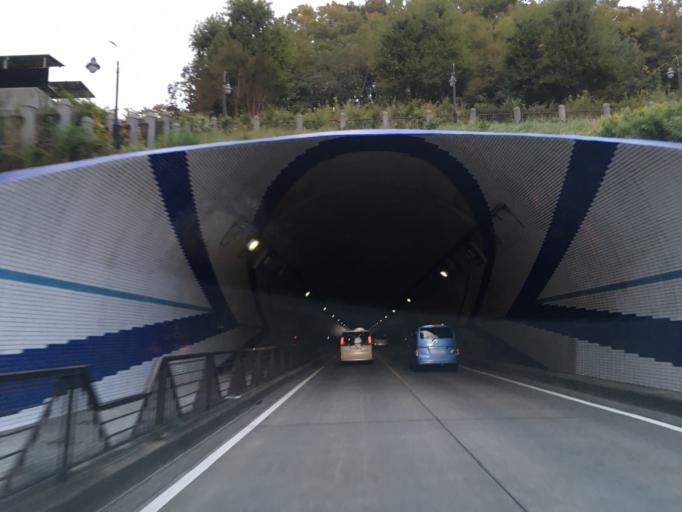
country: JP
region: Tokyo
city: Hachioji
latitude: 35.6044
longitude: 139.3676
